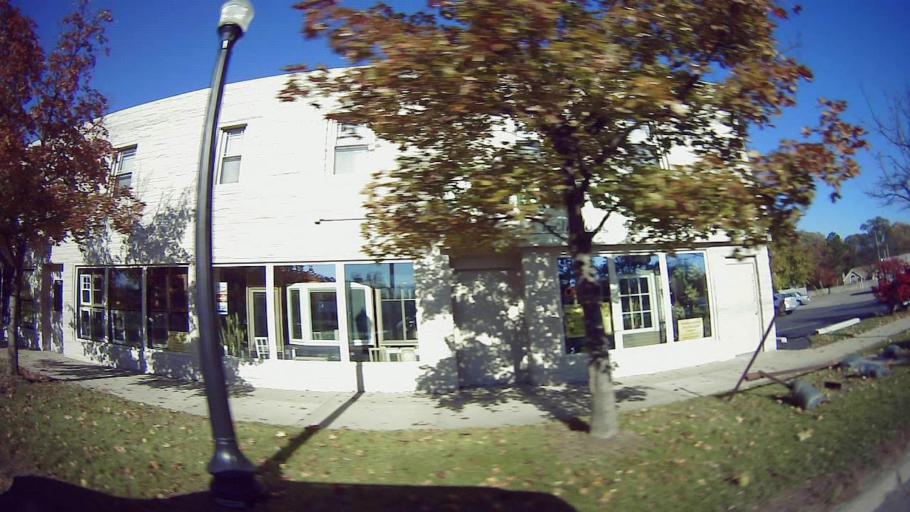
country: US
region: Michigan
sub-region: Oakland County
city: Farmington
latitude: 42.4478
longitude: -83.3351
